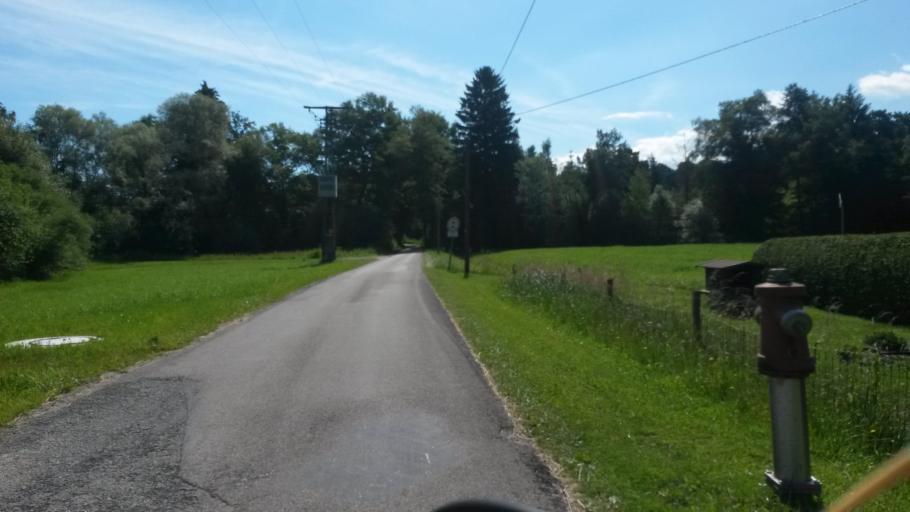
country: DE
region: Bavaria
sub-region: Upper Bavaria
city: Bernau am Chiemsee
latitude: 47.8332
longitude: 12.4000
